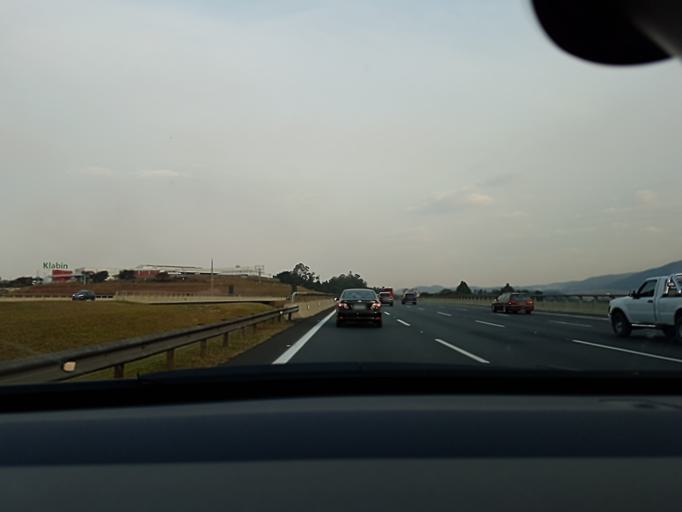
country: BR
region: Sao Paulo
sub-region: Jundiai
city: Jundiai
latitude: -23.1714
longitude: -46.9393
